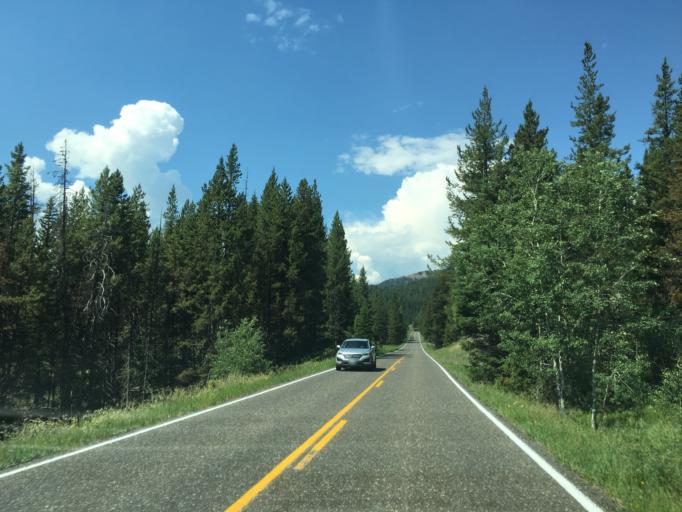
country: US
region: Montana
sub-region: Park County
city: Livingston
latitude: 44.9170
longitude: -110.1063
